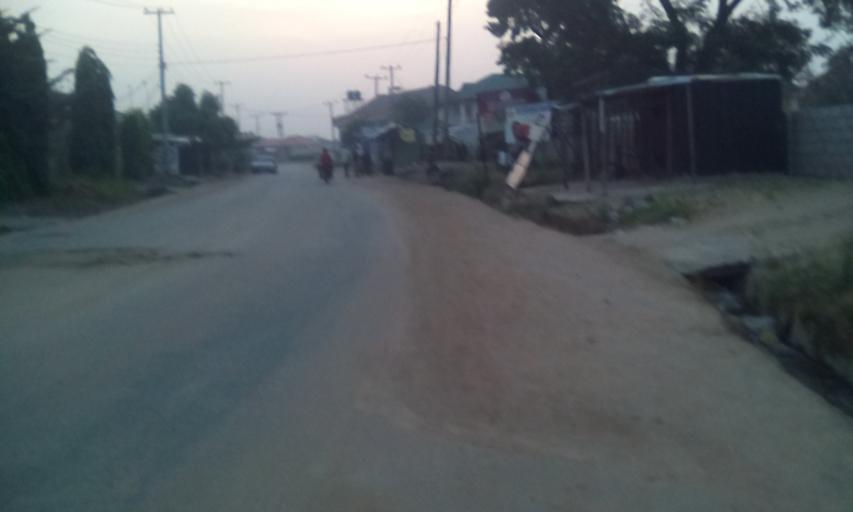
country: NG
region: Abuja Federal Capital Territory
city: Abuja
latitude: 8.9839
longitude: 7.3544
